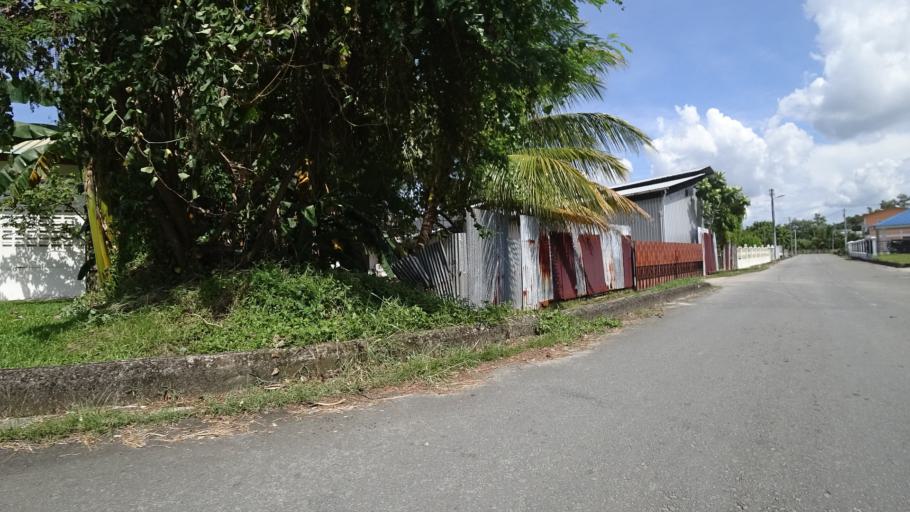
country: BN
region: Brunei and Muara
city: Bandar Seri Begawan
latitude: 4.8915
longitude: 114.8477
